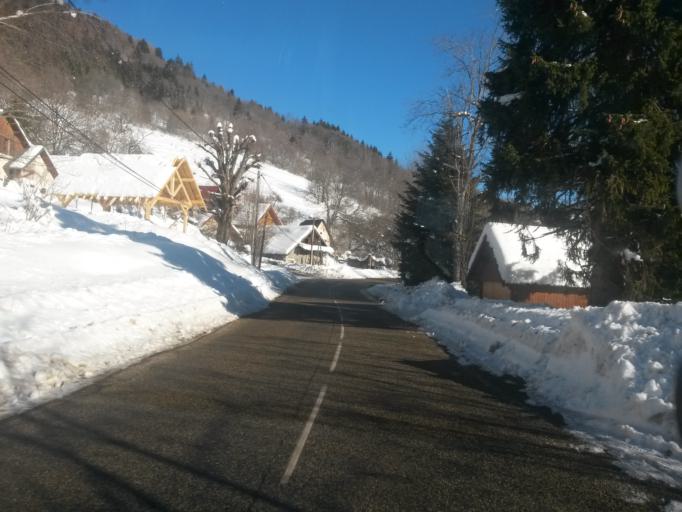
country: FR
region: Rhone-Alpes
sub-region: Departement de l'Isere
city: La Terrasse
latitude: 45.3461
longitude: 5.9082
